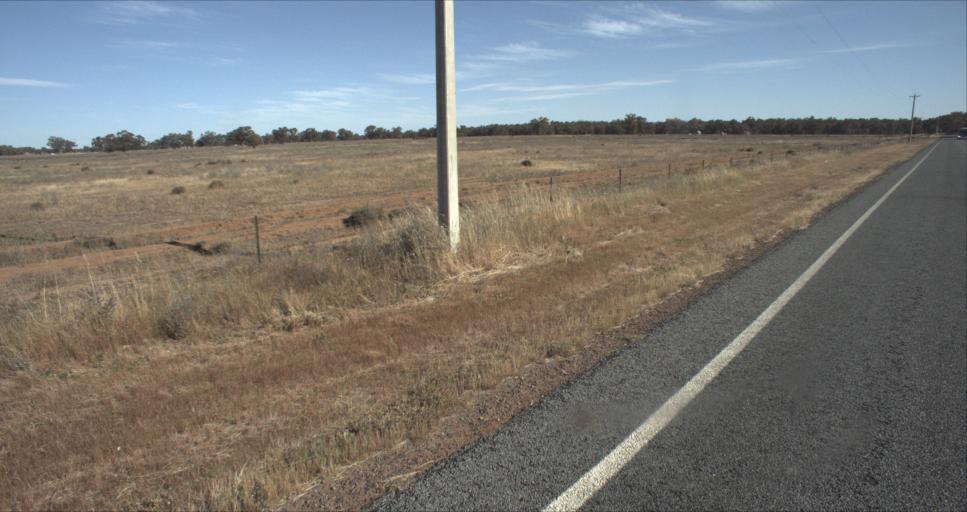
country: AU
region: New South Wales
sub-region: Leeton
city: Leeton
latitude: -34.6183
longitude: 146.3991
